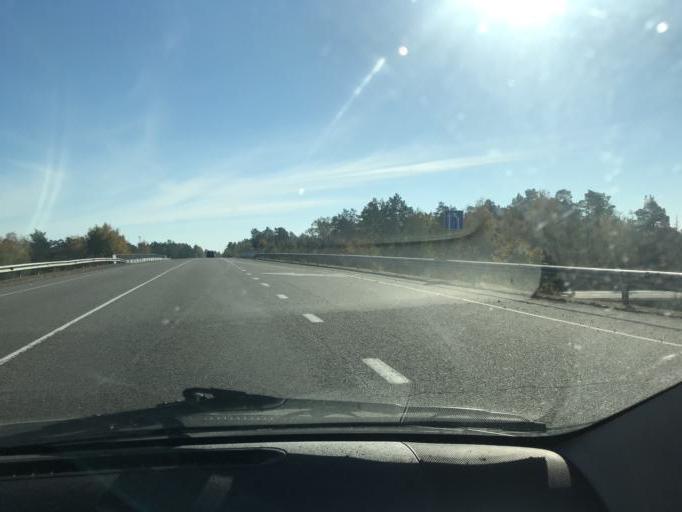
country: BY
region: Brest
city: Mikashevichy
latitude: 52.2447
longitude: 27.4438
